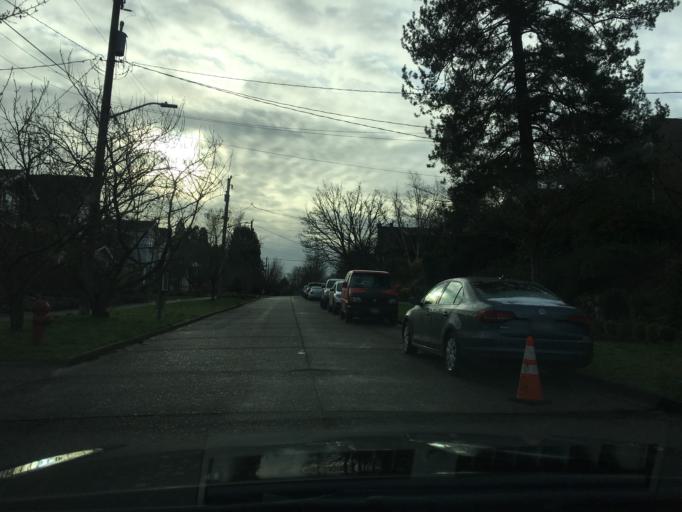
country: US
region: Washington
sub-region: King County
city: Seattle
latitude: 47.6685
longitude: -122.3314
